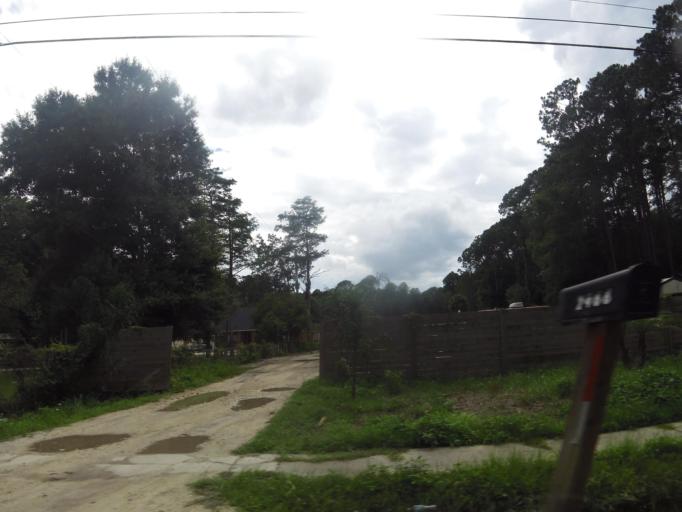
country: US
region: Florida
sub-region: Duval County
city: Jacksonville
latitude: 30.2933
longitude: -81.5291
